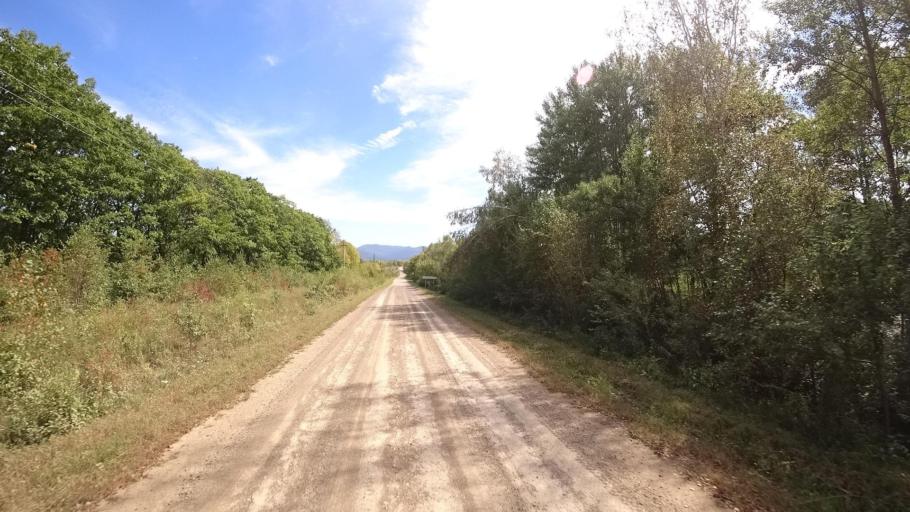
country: RU
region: Primorskiy
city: Yakovlevka
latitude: 44.7106
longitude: 133.6272
